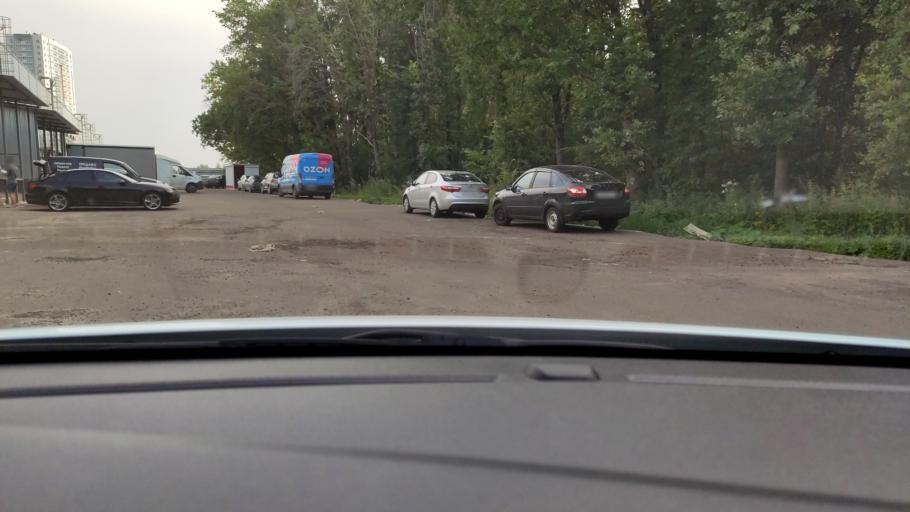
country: RU
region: Tatarstan
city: Stolbishchi
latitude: 55.7259
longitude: 49.1879
